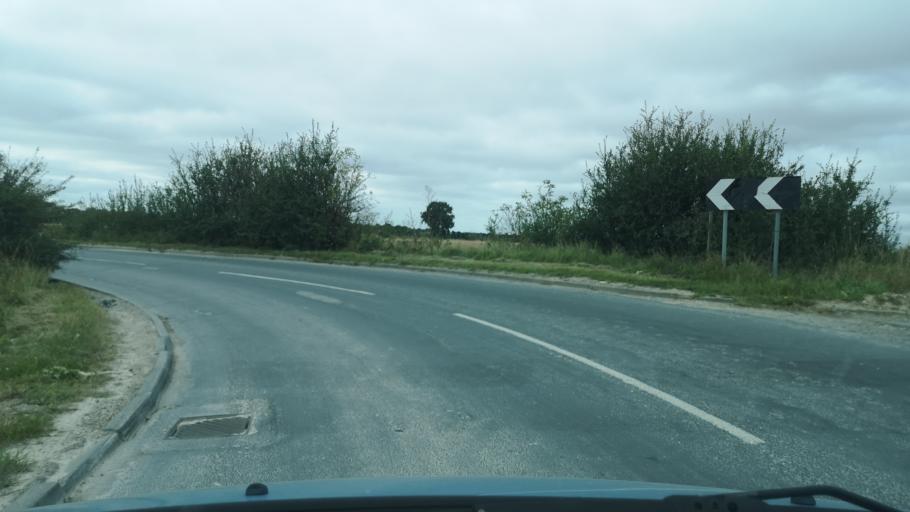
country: GB
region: England
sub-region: City and Borough of Wakefield
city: Knottingley
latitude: 53.6861
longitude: -1.2430
